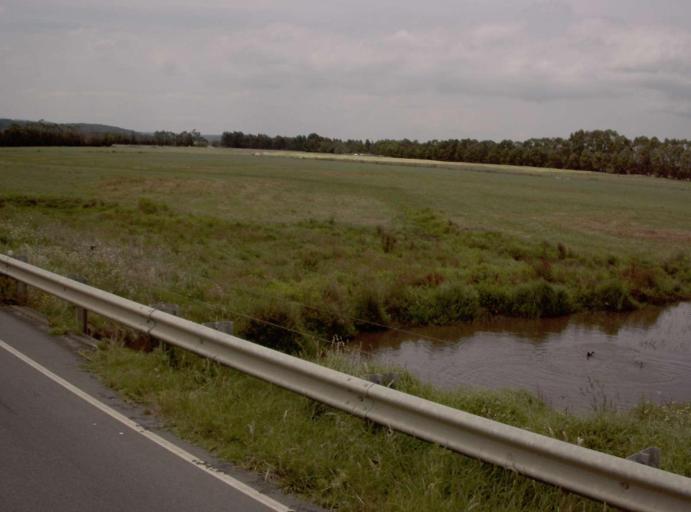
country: AU
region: Victoria
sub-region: Latrobe
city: Traralgon
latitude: -38.5082
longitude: 146.6635
